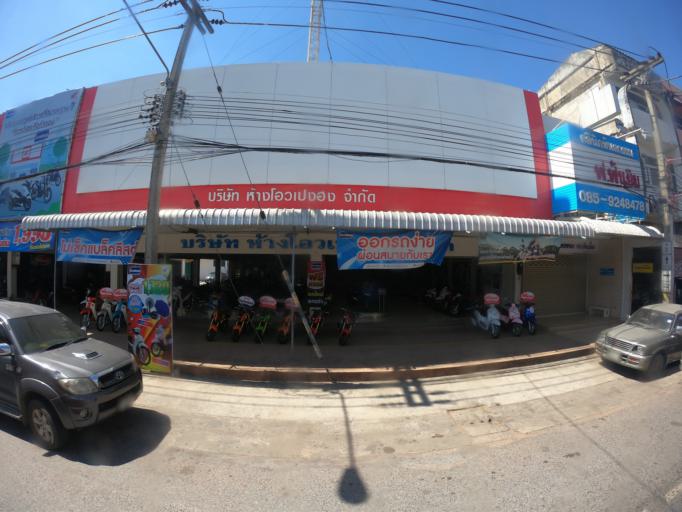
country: TH
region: Khon Kaen
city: Ban Phai
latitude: 16.0586
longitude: 102.7261
